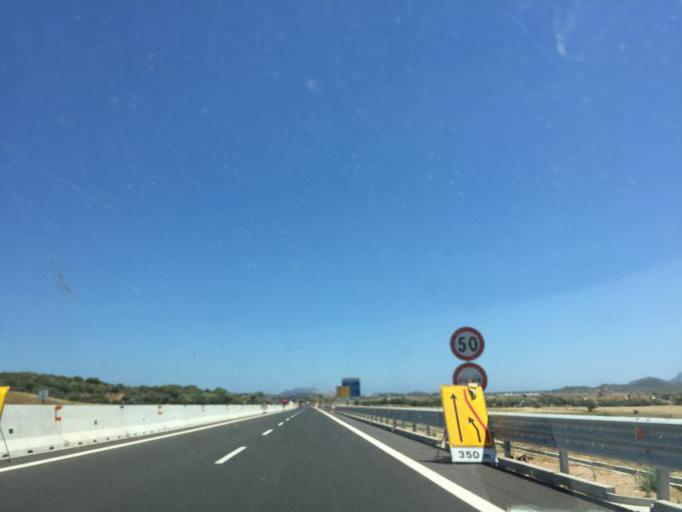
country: IT
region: Sardinia
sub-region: Provincia di Olbia-Tempio
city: Olbia
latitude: 40.8883
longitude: 9.4790
